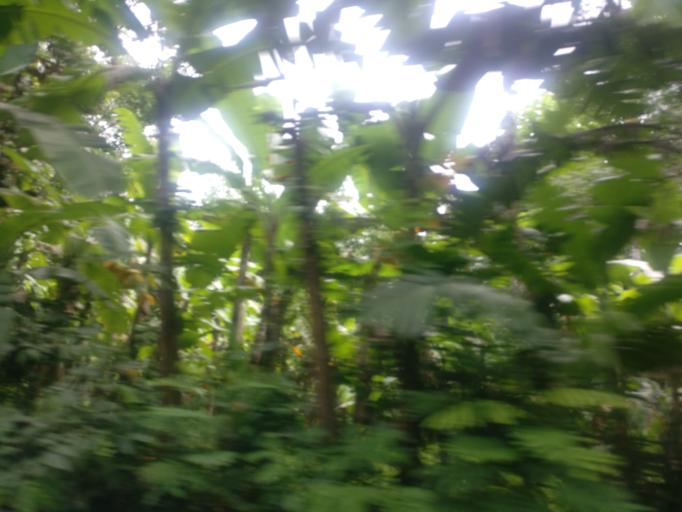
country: ID
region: Bali
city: Banjar Kawan
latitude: -8.4878
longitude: 115.5160
